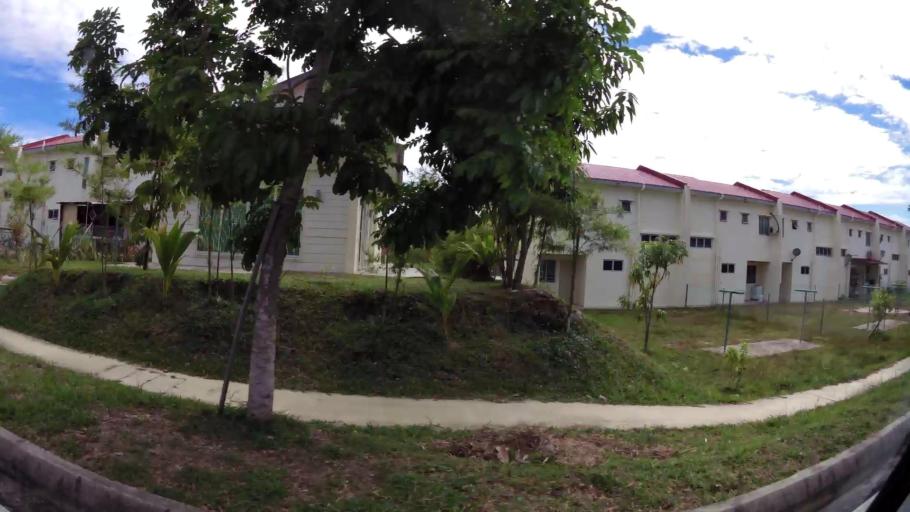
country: BN
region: Brunei and Muara
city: Bandar Seri Begawan
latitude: 4.9735
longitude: 115.0064
